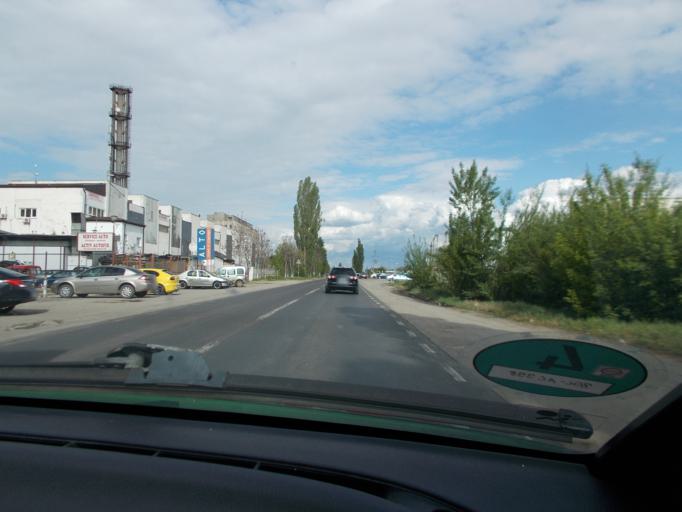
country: RO
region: Ilfov
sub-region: Comuna Cernica
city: Caldararu
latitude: 44.4517
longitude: 26.2434
